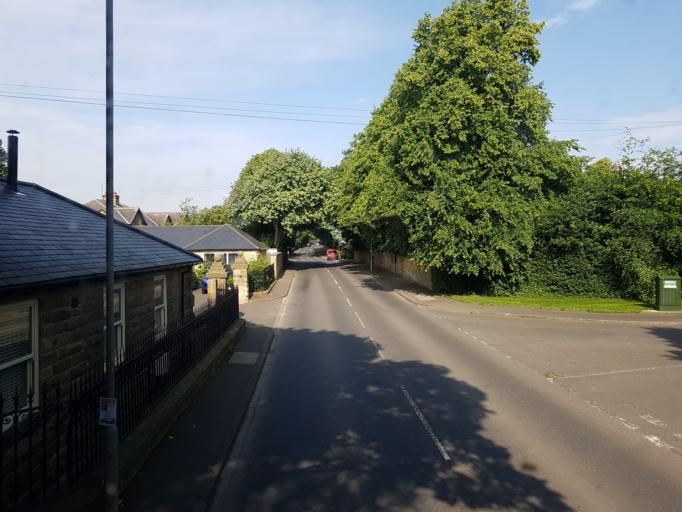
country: GB
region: England
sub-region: Northumberland
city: Alnwick
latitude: 55.4080
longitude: -1.6893
